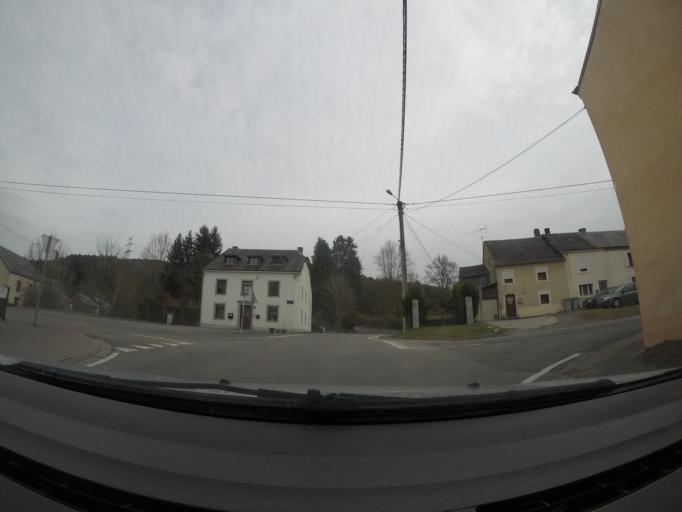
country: BE
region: Wallonia
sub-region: Province du Luxembourg
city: Martelange
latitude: 49.8425
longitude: 5.7226
